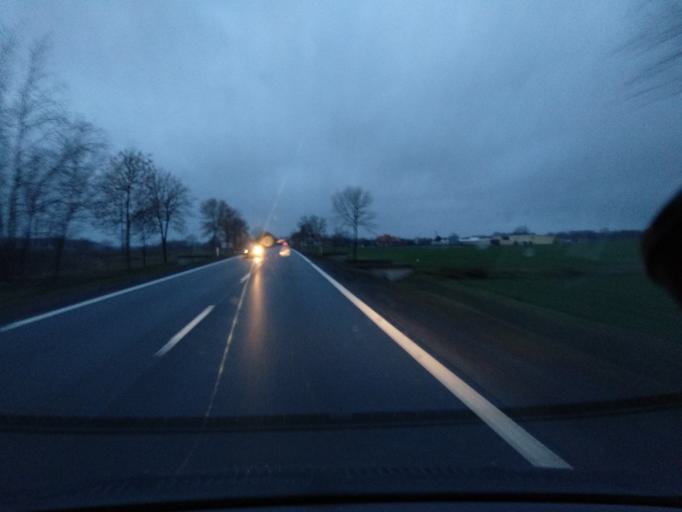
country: PL
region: Lower Silesian Voivodeship
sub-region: Powiat sredzki
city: Malczyce
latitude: 51.1976
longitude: 16.4899
